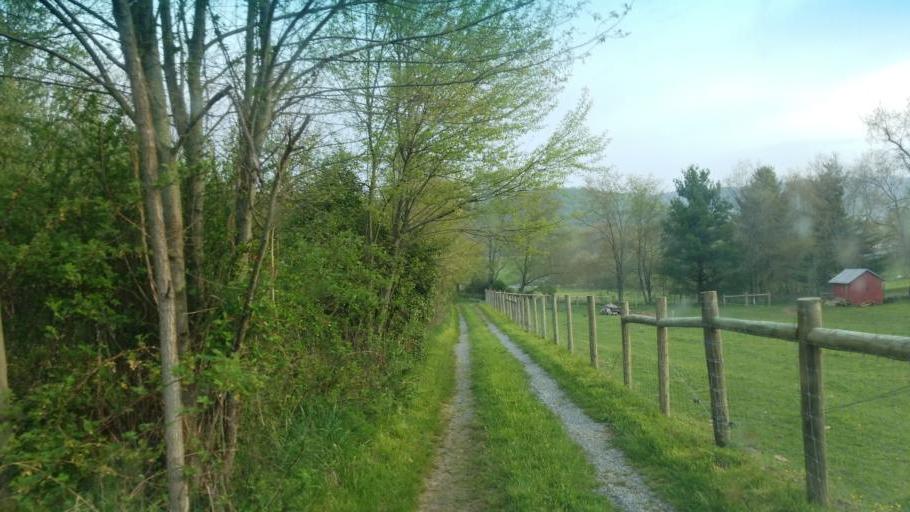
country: US
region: Virginia
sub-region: Smyth County
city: Marion
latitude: 36.7558
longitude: -81.4731
